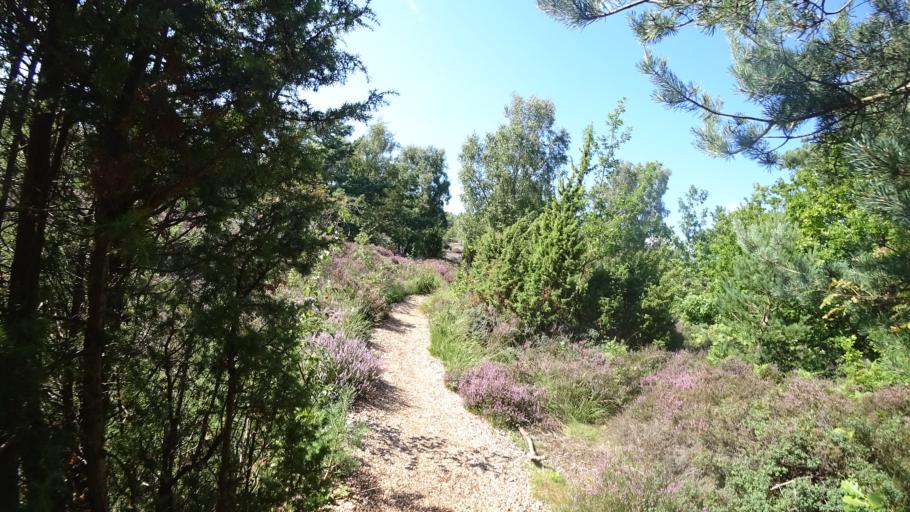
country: SE
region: Vaestra Goetaland
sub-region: Goteborg
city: Styrso
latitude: 57.6088
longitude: 11.7818
